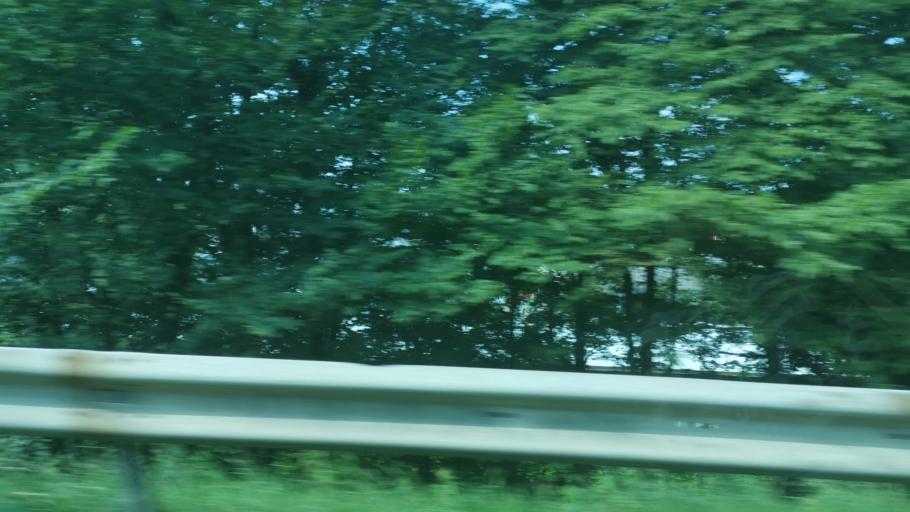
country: DE
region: Bavaria
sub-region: Upper Palatinate
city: Cham
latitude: 49.2250
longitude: 12.6776
